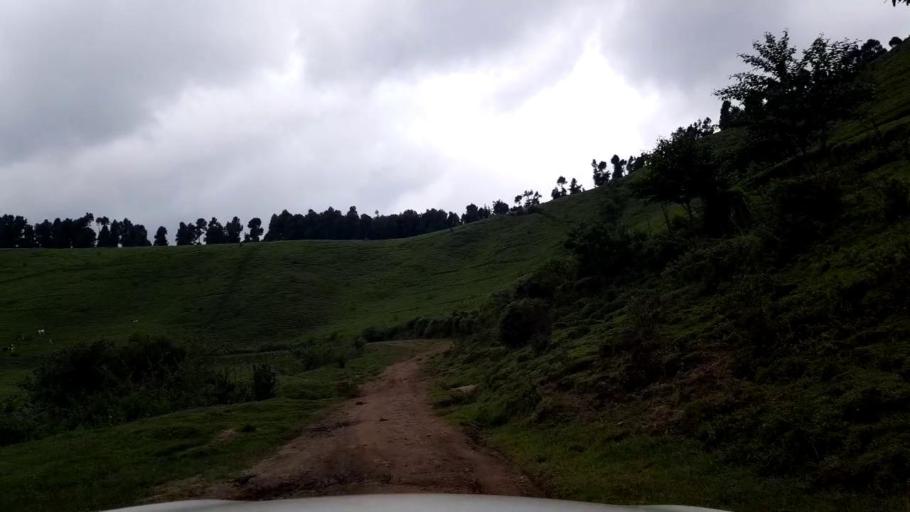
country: RW
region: Western Province
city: Gisenyi
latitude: -1.6926
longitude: 29.4249
